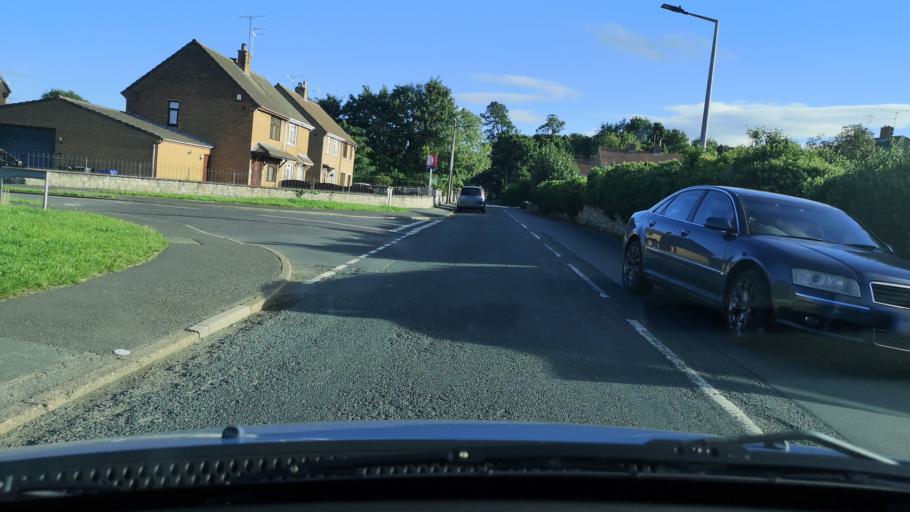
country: GB
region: England
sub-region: Doncaster
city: Campsall
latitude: 53.6228
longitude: -1.1793
